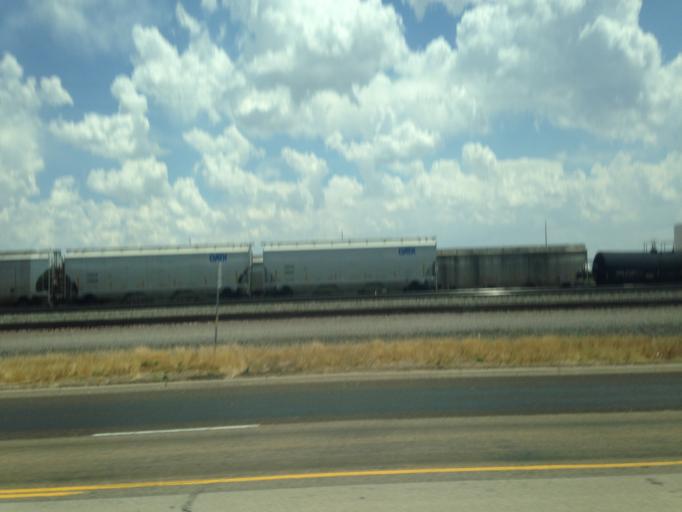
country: US
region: Texas
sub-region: Deaf Smith County
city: Hereford
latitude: 34.8249
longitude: -102.3777
